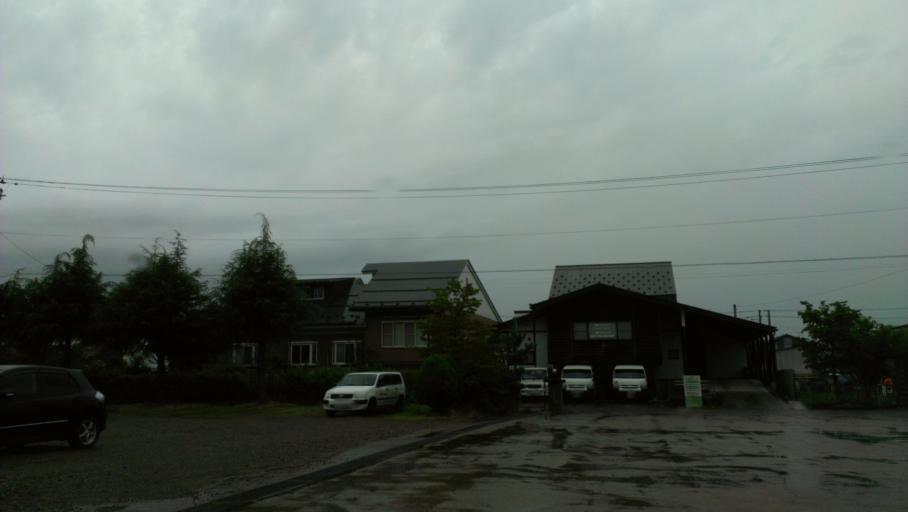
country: JP
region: Fukushima
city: Kitakata
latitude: 37.5229
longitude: 139.8742
